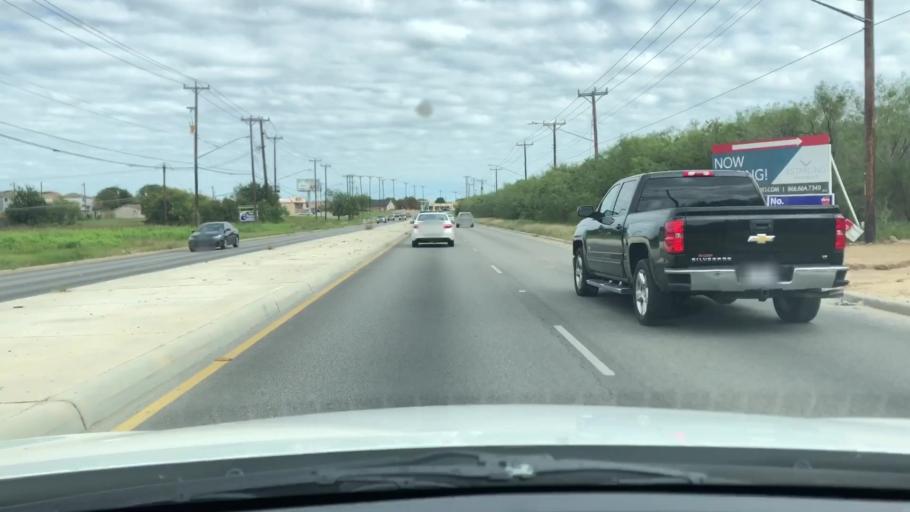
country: US
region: Texas
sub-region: Bexar County
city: Leon Valley
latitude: 29.4901
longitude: -98.6885
